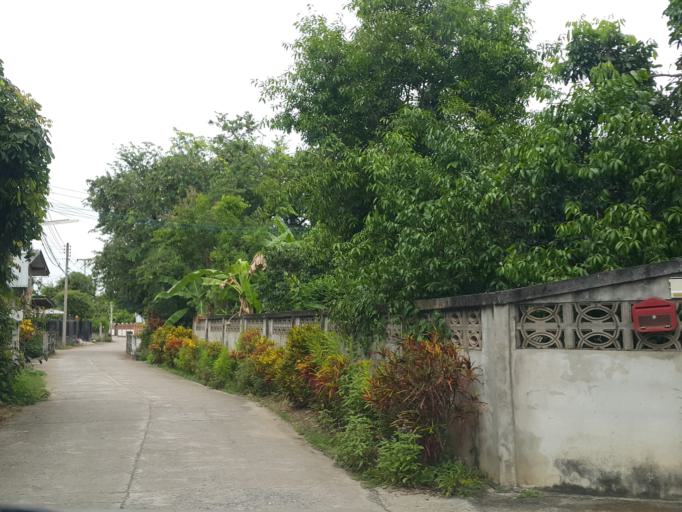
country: TH
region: Chiang Mai
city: San Sai
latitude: 18.8398
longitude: 99.1245
